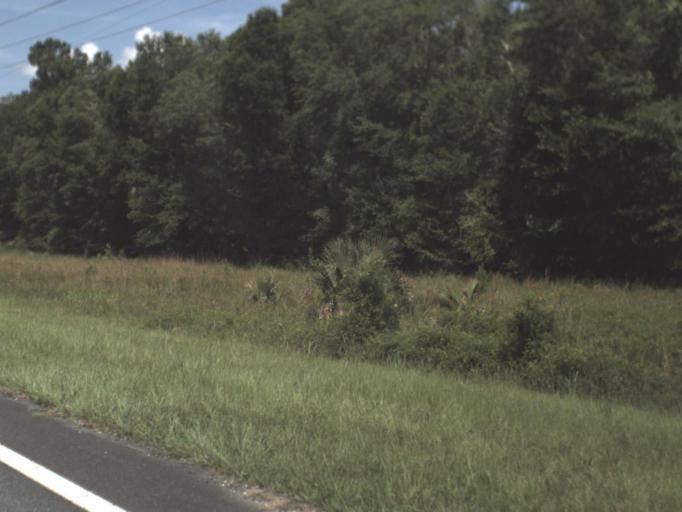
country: US
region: Florida
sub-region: Levy County
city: Chiefland
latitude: 29.3203
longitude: -82.7817
